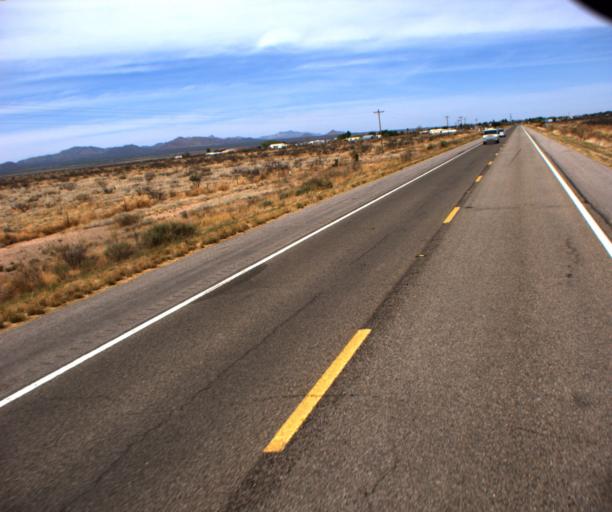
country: US
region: Arizona
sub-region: Cochise County
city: Pirtleville
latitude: 31.6638
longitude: -109.6795
